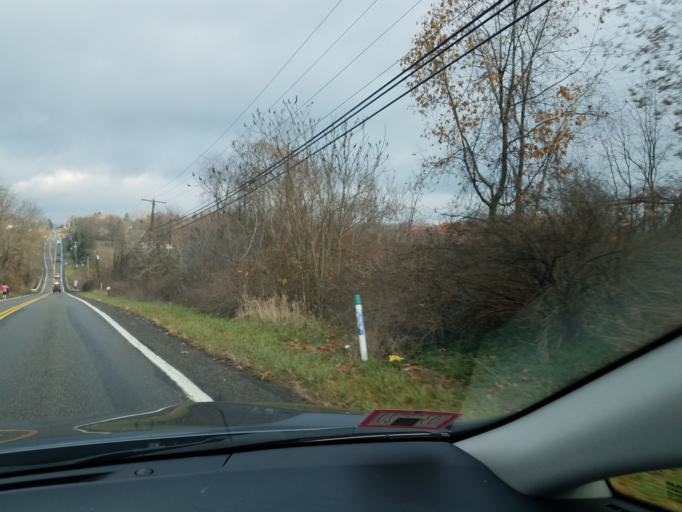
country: US
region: Pennsylvania
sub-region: Allegheny County
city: Franklin Park
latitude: 40.6044
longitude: -80.0994
